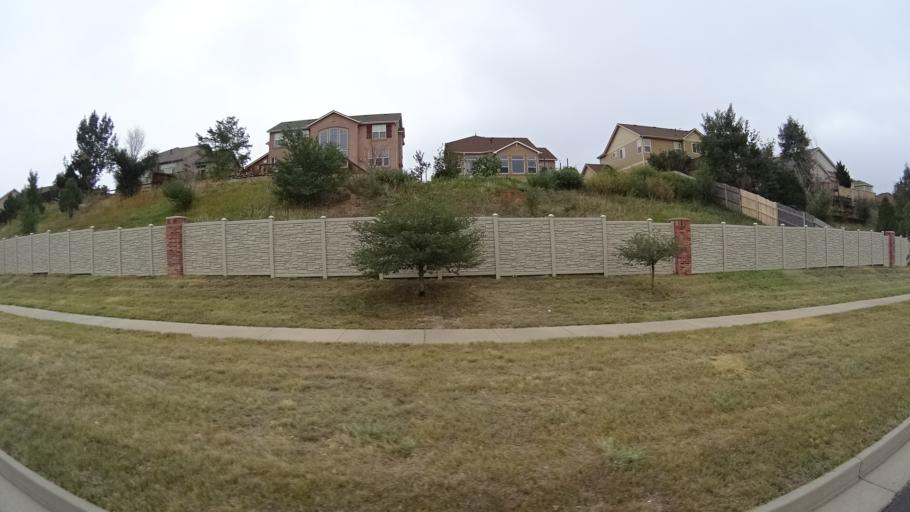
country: US
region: Colorado
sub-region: El Paso County
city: Cimarron Hills
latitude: 38.9005
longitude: -104.6967
